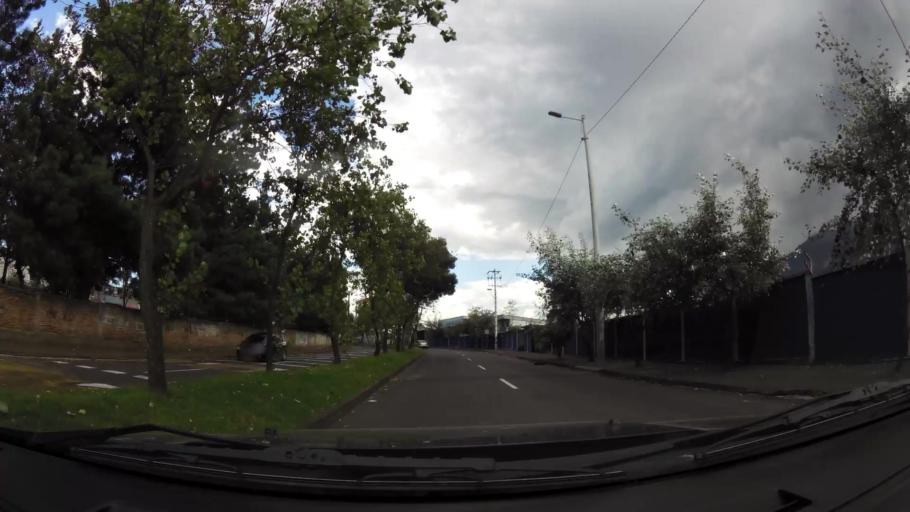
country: EC
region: Pichincha
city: Quito
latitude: -0.1271
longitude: -78.4893
